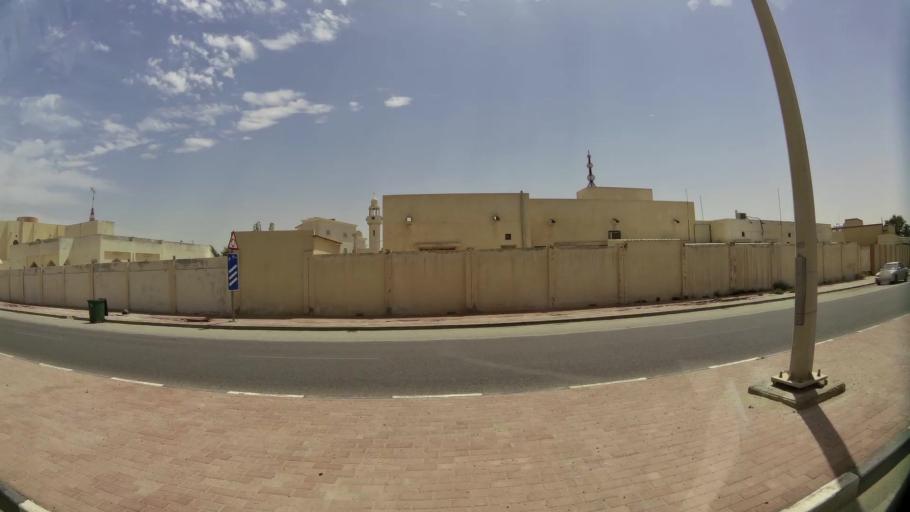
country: QA
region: Baladiyat ar Rayyan
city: Ar Rayyan
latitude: 25.2996
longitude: 51.4086
